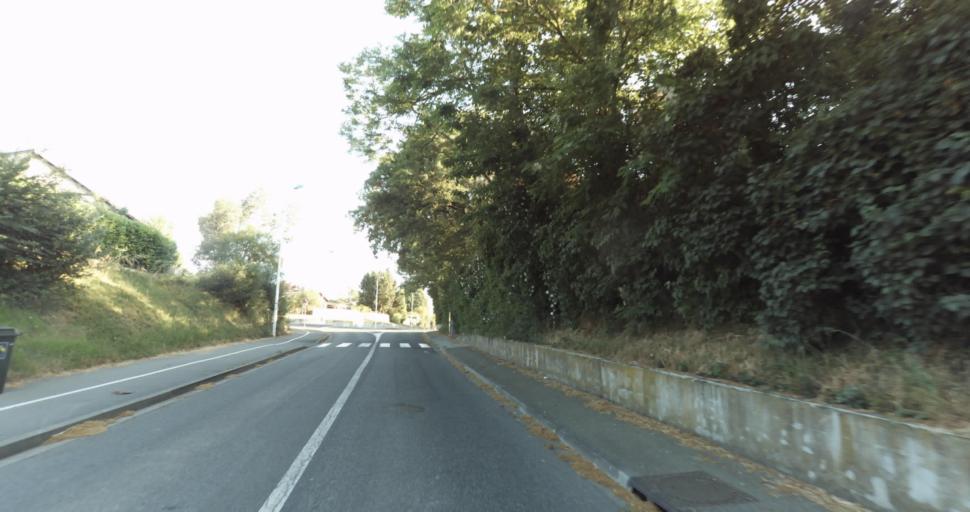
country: FR
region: Midi-Pyrenees
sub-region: Departement de la Haute-Garonne
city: Leguevin
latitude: 43.6024
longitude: 1.2332
